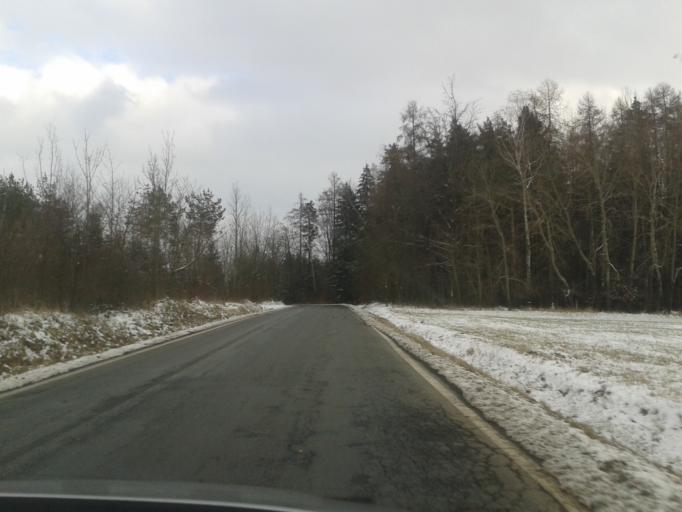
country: CZ
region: Olomoucky
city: Konice
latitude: 49.5891
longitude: 16.8565
